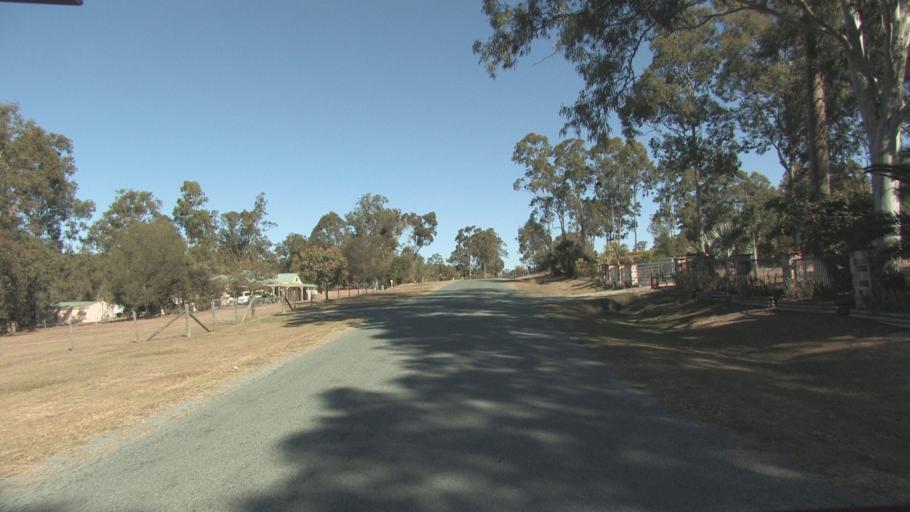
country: AU
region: Queensland
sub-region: Logan
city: Cedar Vale
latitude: -27.8619
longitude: 153.0352
